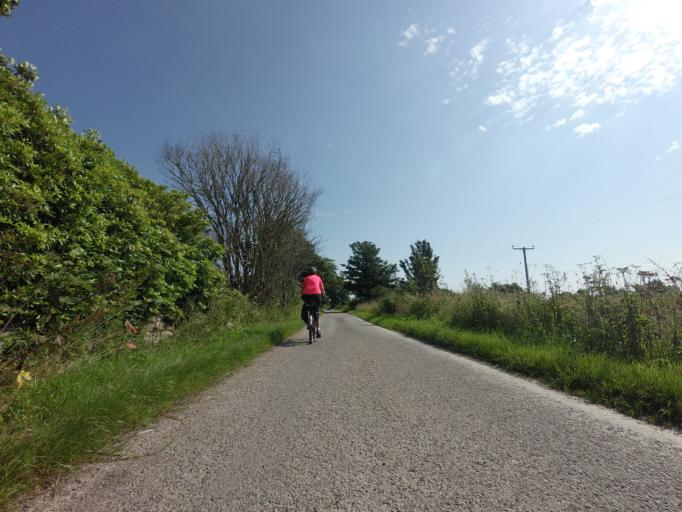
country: GB
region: Scotland
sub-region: Highland
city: Invergordon
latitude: 57.7220
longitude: -4.2046
